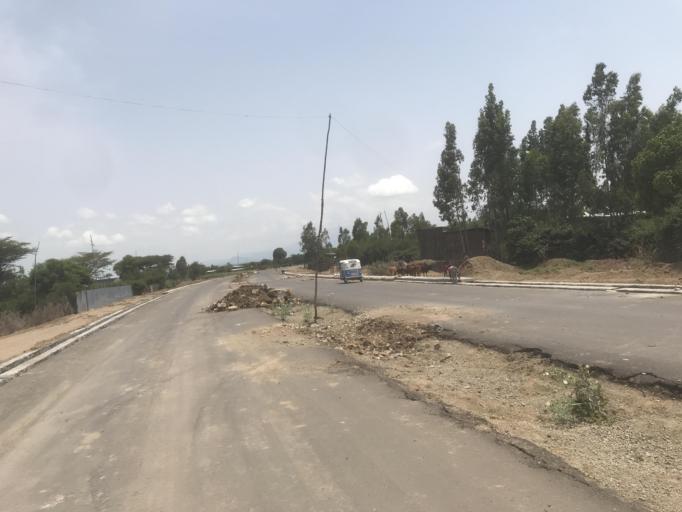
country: ET
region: Oromiya
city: Mojo
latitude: 8.2921
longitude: 38.9412
